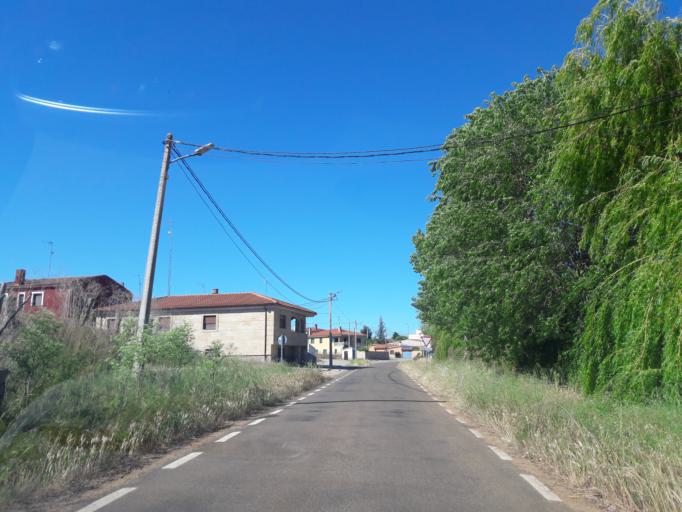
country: ES
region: Castille and Leon
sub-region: Provincia de Salamanca
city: Parada de Arriba
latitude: 40.9881
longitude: -5.7934
